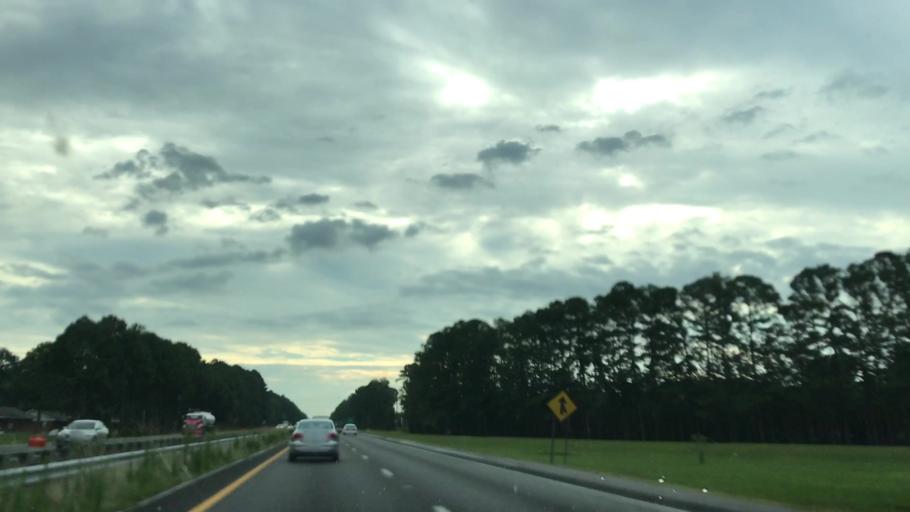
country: US
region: North Carolina
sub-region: Johnston County
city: Smithfield
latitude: 35.4922
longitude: -78.3453
